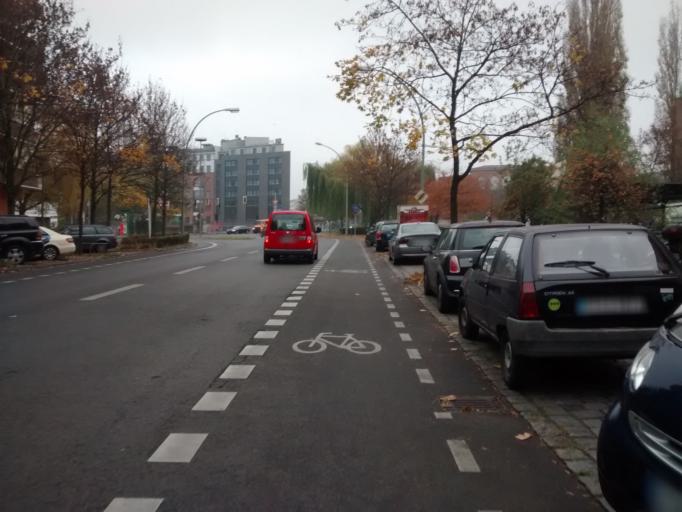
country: DE
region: Berlin
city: Moabit
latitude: 52.5215
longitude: 13.3283
